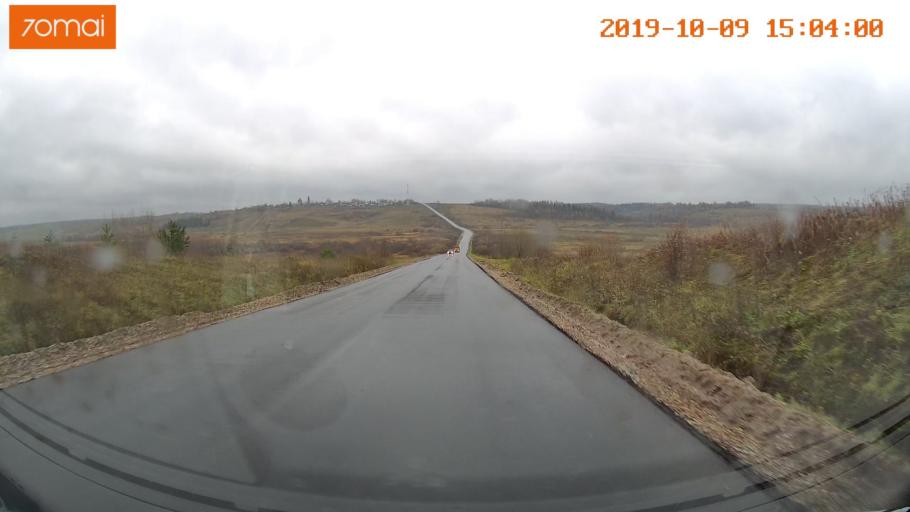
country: RU
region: Kostroma
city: Chistyye Bory
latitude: 58.2641
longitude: 41.6712
